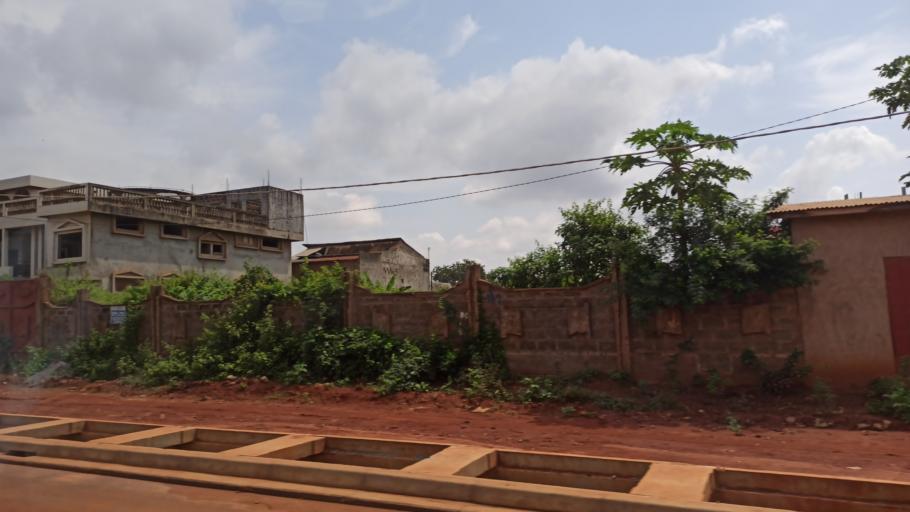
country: BJ
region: Queme
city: Porto-Novo
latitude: 6.4941
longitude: 2.5897
